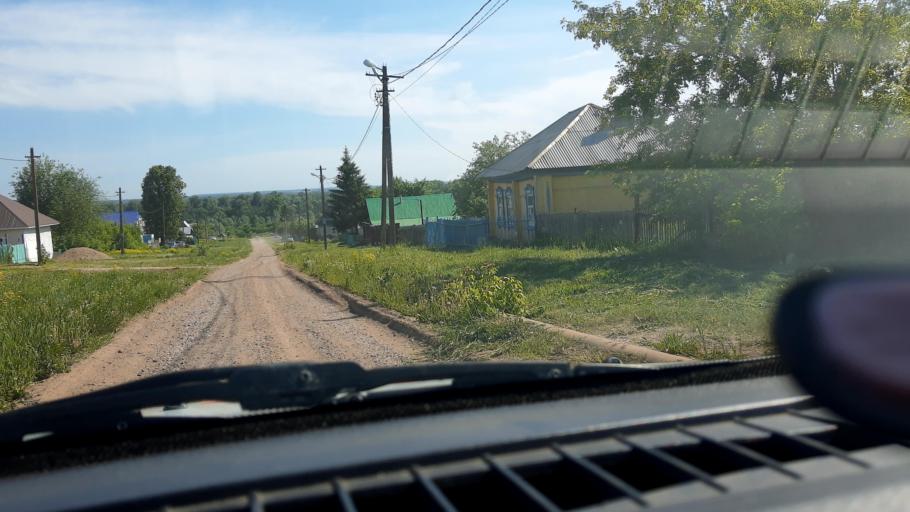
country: RU
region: Bashkortostan
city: Iglino
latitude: 54.8836
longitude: 56.3061
